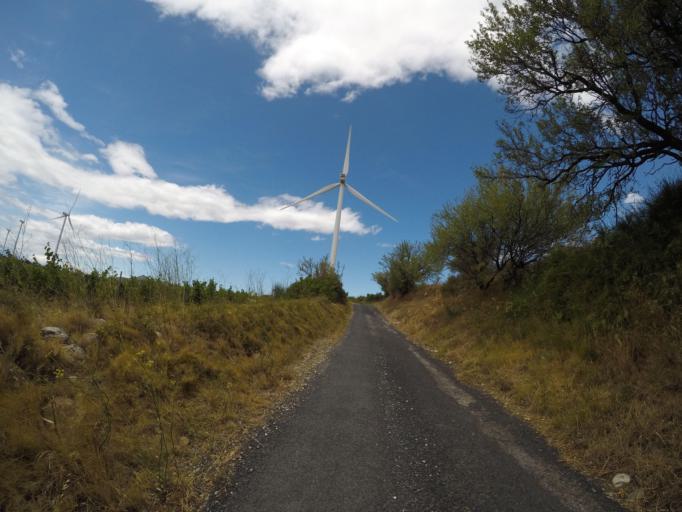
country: FR
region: Languedoc-Roussillon
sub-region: Departement des Pyrenees-Orientales
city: Pezilla-la-Riviere
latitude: 42.7174
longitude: 2.7621
